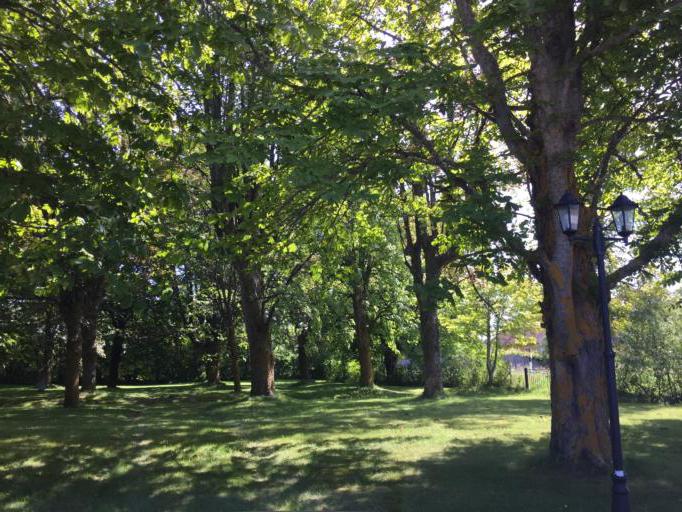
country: SE
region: Gotland
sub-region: Gotland
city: Klintehamn
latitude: 57.4478
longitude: 18.1411
